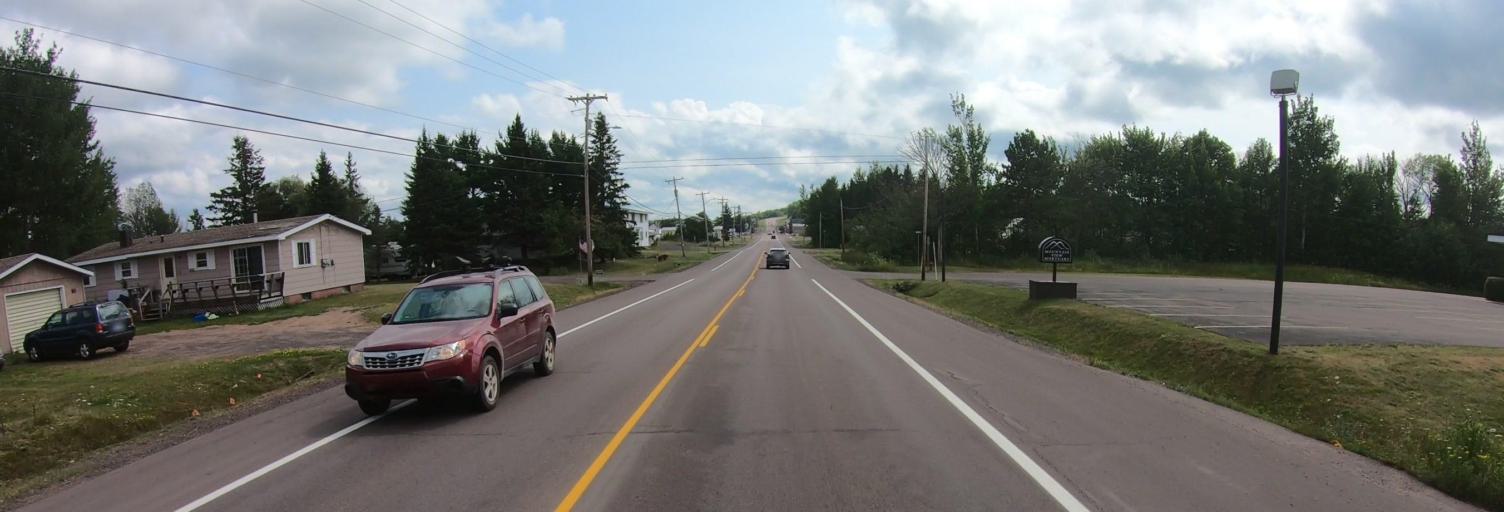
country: US
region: Michigan
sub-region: Houghton County
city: Hancock
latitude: 47.0756
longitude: -88.6405
